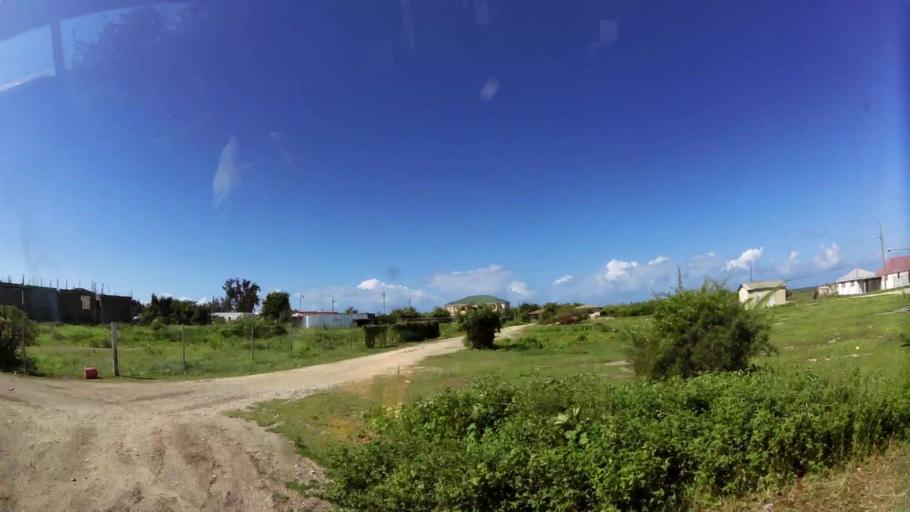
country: AG
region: Barbuda
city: Codrington
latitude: 17.6423
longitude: -61.8256
